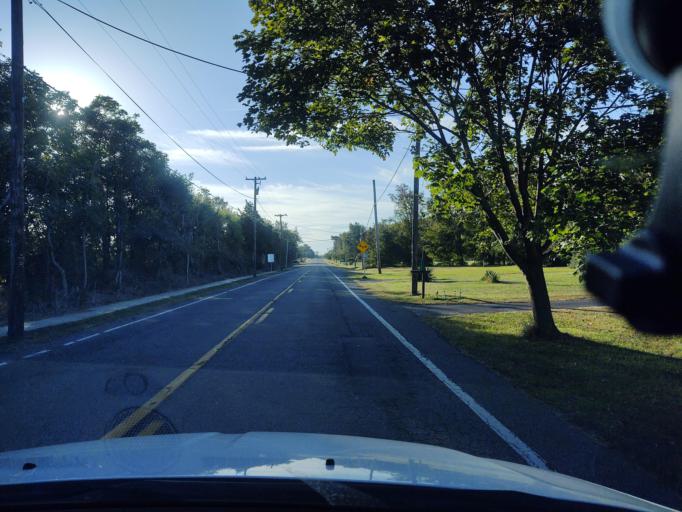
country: US
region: Maryland
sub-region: Queen Anne's County
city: Kingstown
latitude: 39.2389
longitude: -75.9199
